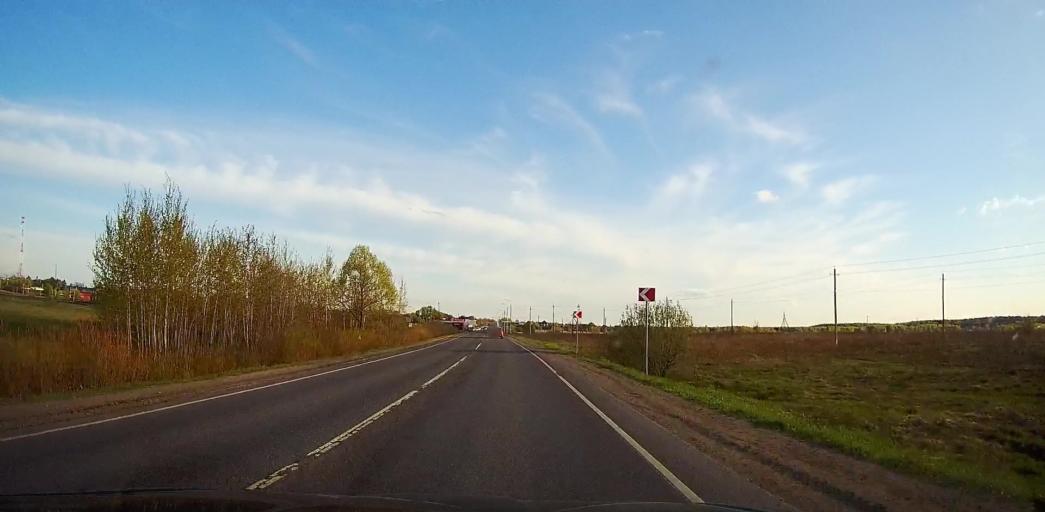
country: RU
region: Moskovskaya
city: Bronnitsy
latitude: 55.3333
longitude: 38.2196
